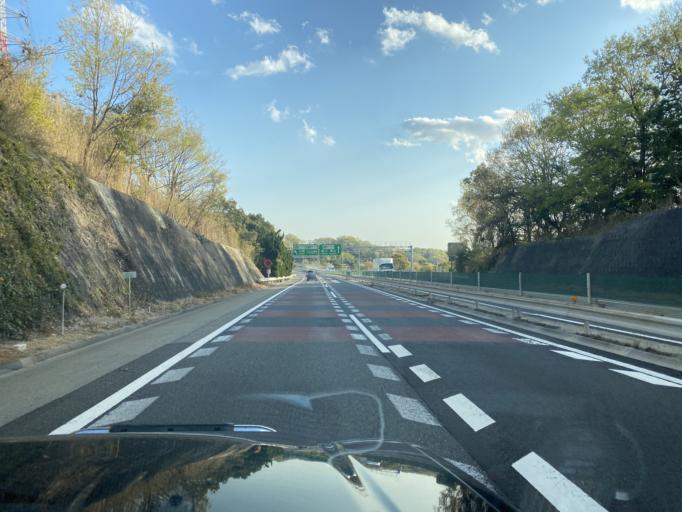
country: JP
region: Hyogo
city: Sandacho
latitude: 34.8981
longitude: 135.1532
